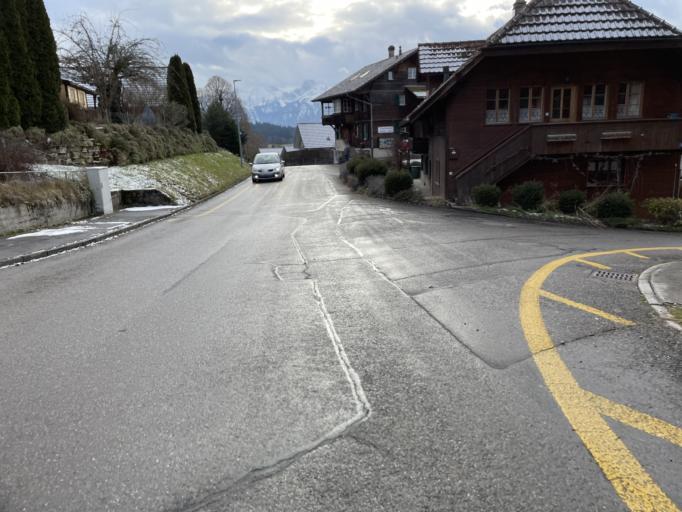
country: CH
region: Lucerne
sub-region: Entlebuch District
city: Oberdiessbach
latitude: 46.8244
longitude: 7.6147
